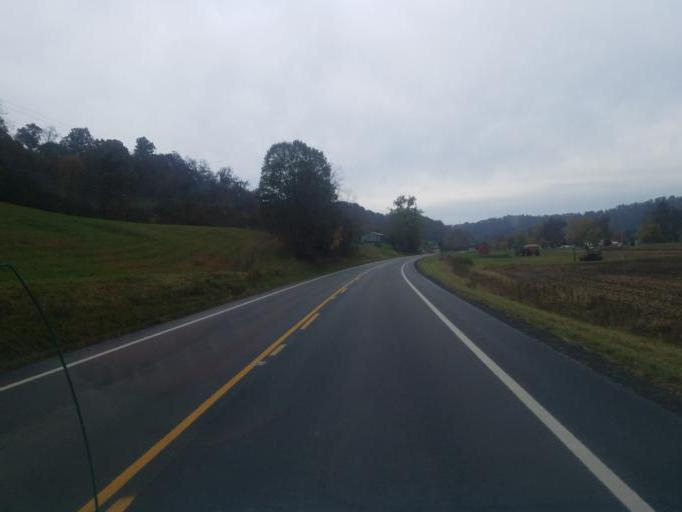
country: US
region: Ohio
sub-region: Washington County
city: Beverly
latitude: 39.5465
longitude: -81.5486
